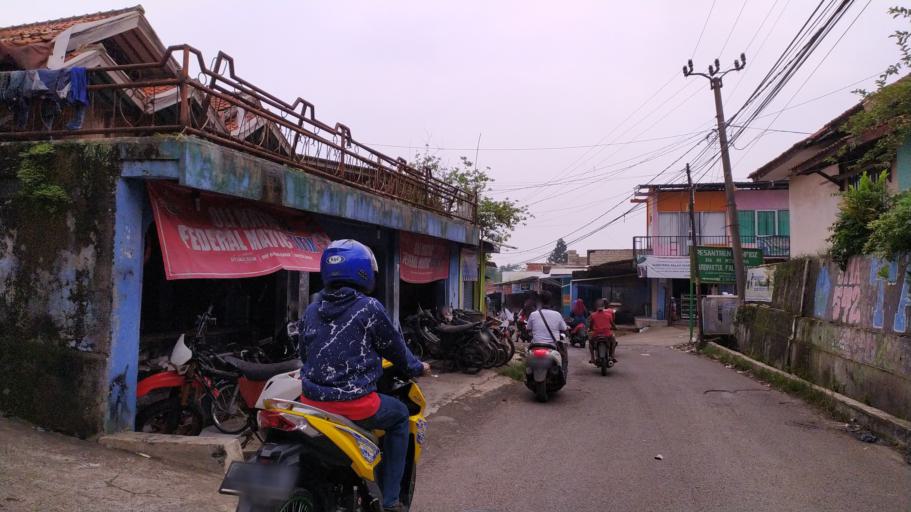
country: ID
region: West Java
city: Ciampea
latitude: -6.5859
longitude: 106.7059
